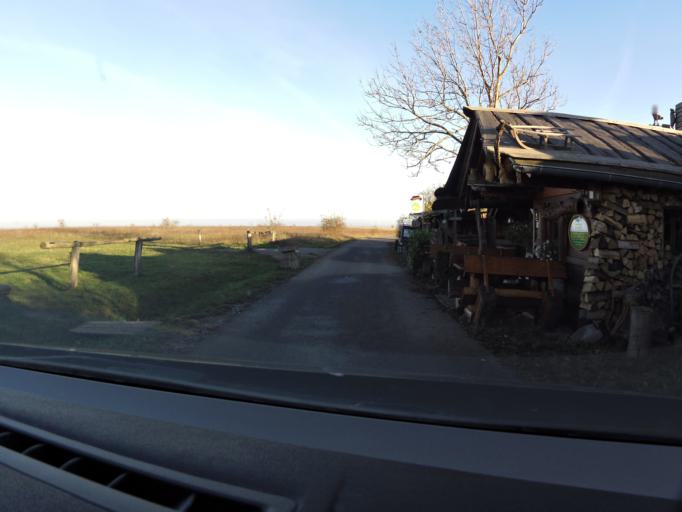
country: DE
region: Thuringia
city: Weberstedt
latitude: 51.0681
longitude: 10.4638
